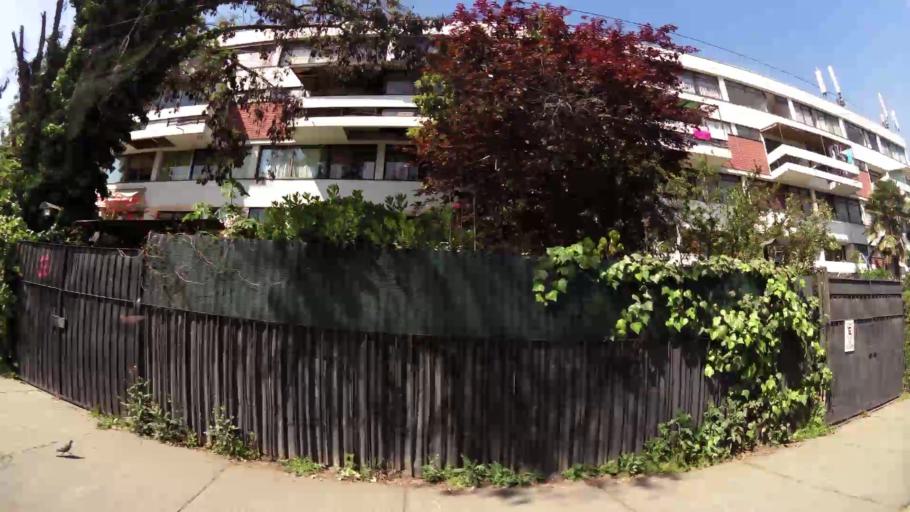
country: CL
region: Santiago Metropolitan
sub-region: Provincia de Santiago
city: Villa Presidente Frei, Nunoa, Santiago, Chile
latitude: -33.4604
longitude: -70.5845
